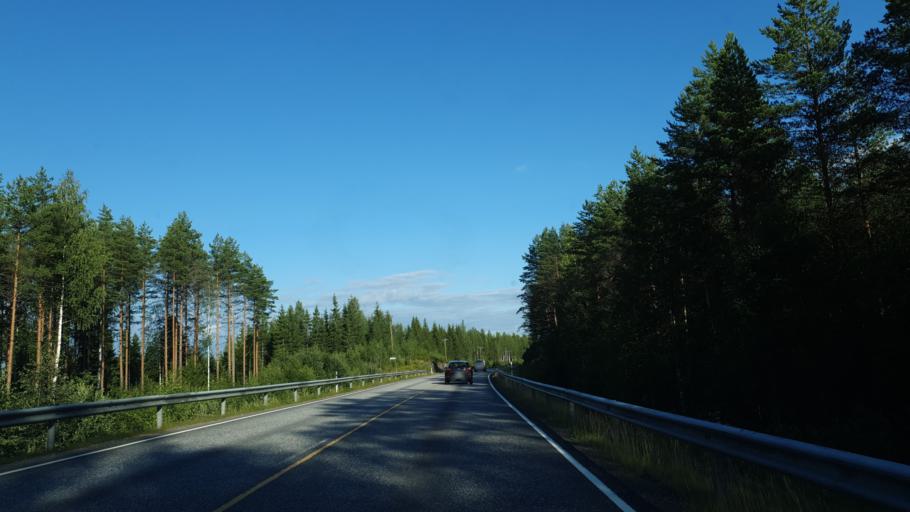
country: FI
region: North Karelia
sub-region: Joensuu
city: Outokumpu
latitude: 62.5315
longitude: 28.9787
